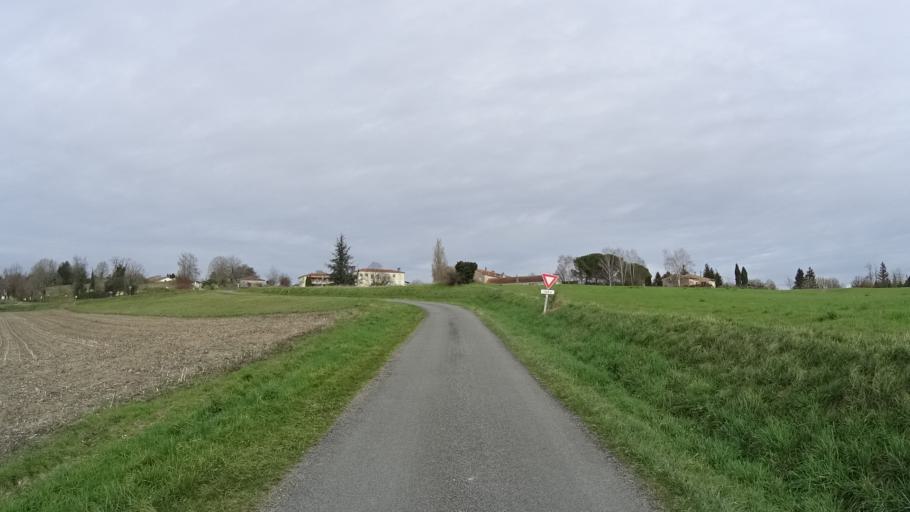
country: FR
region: Aquitaine
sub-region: Departement de la Dordogne
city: Saint-Aulaye
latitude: 45.2650
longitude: 0.1687
